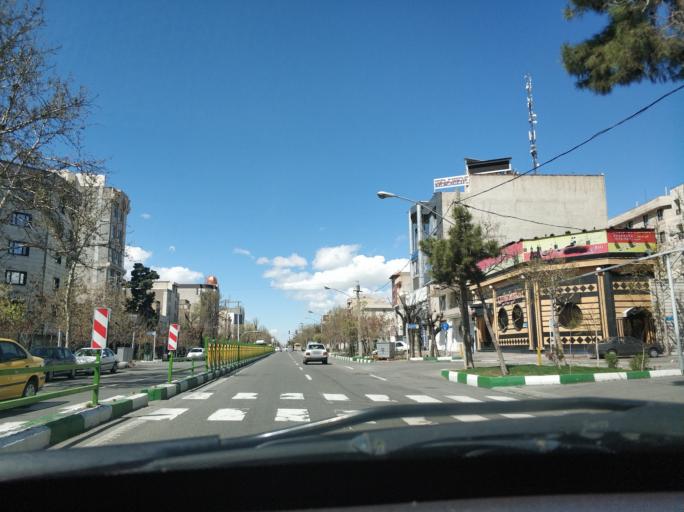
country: IR
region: Tehran
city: Tehran
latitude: 35.7198
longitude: 51.4981
